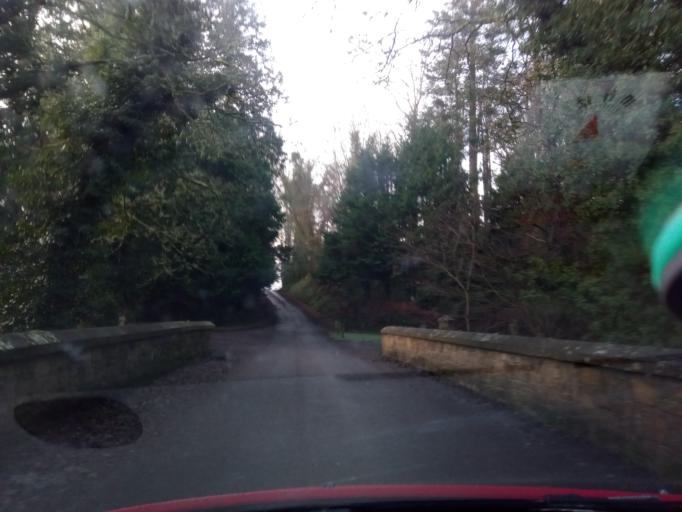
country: GB
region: Scotland
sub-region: The Scottish Borders
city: Hawick
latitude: 55.4581
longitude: -2.7231
